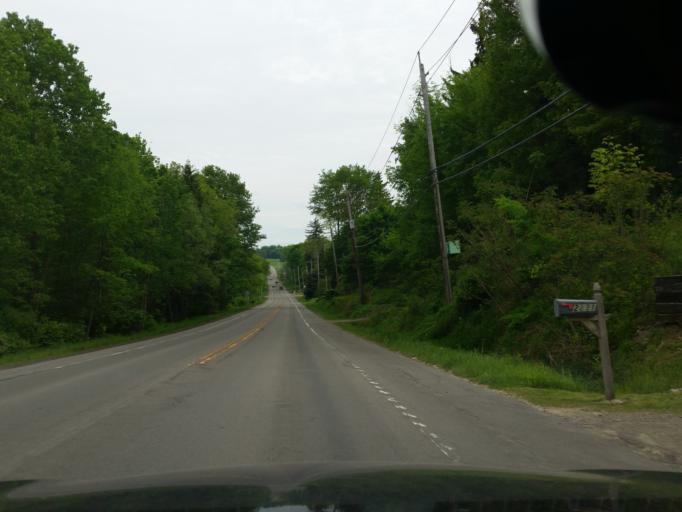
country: US
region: New York
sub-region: Chautauqua County
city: Lakewood
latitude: 42.1207
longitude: -79.3906
